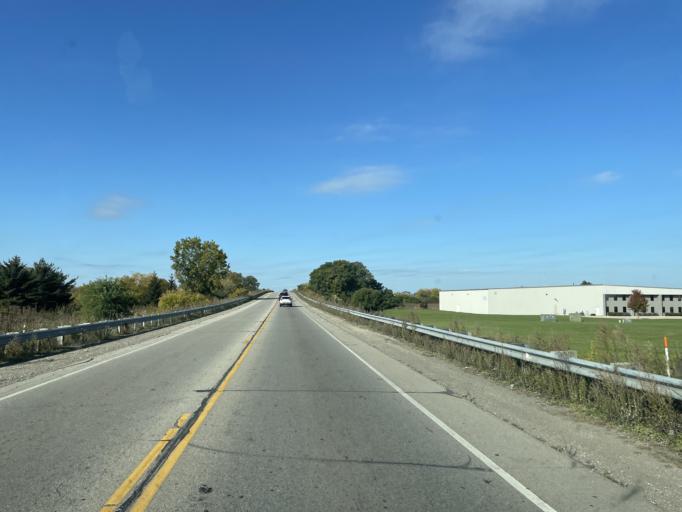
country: US
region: Wisconsin
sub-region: Kenosha County
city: Pleasant Prairie
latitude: 42.5889
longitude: -87.8932
